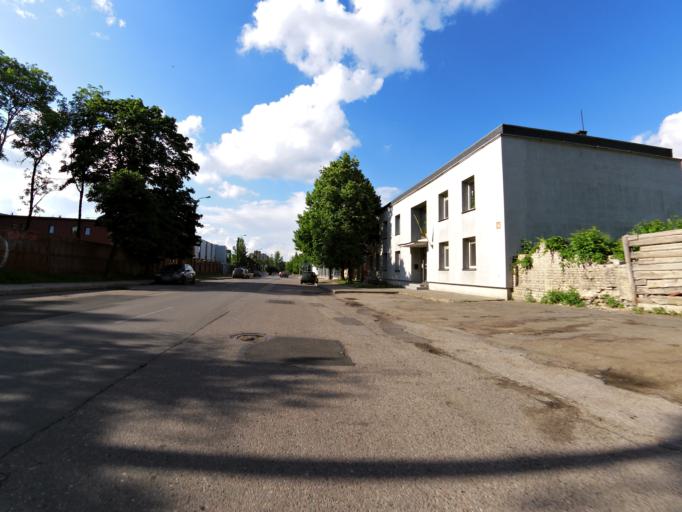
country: LT
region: Vilnius County
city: Naujamiestis
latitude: 54.6688
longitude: 25.2742
